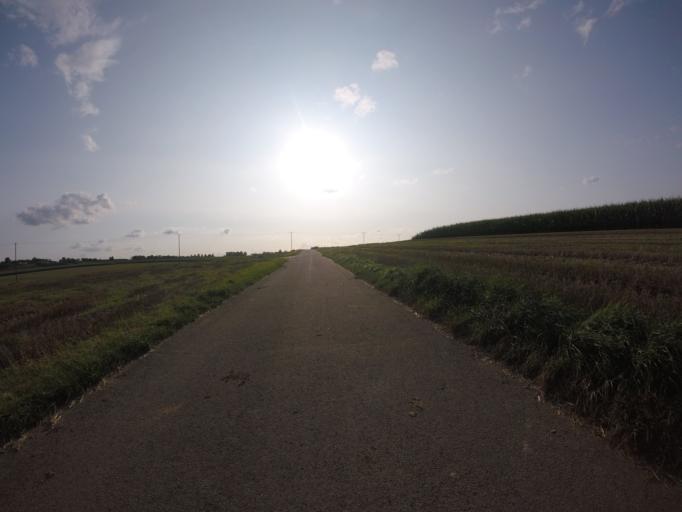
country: DE
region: Baden-Wuerttemberg
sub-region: Regierungsbezirk Stuttgart
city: Aspach
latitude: 48.9634
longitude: 9.4166
